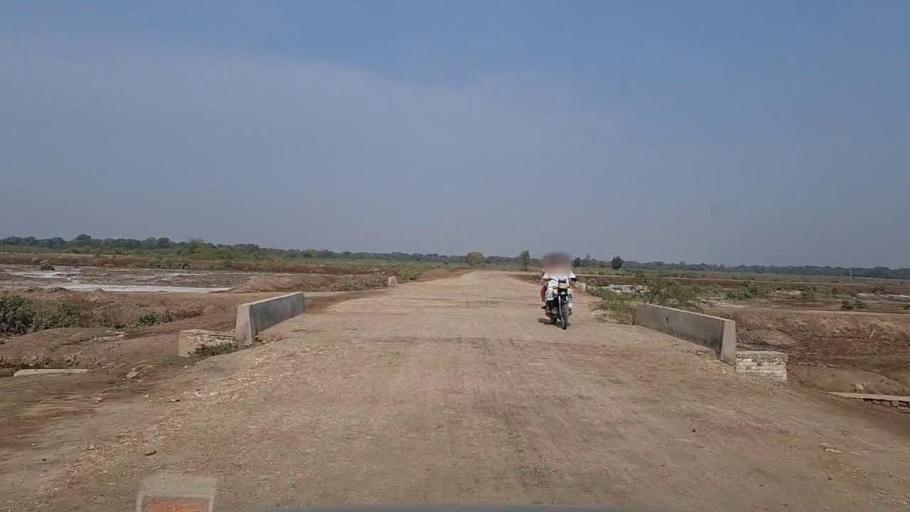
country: PK
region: Sindh
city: Mirwah Gorchani
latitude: 25.3336
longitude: 69.0615
